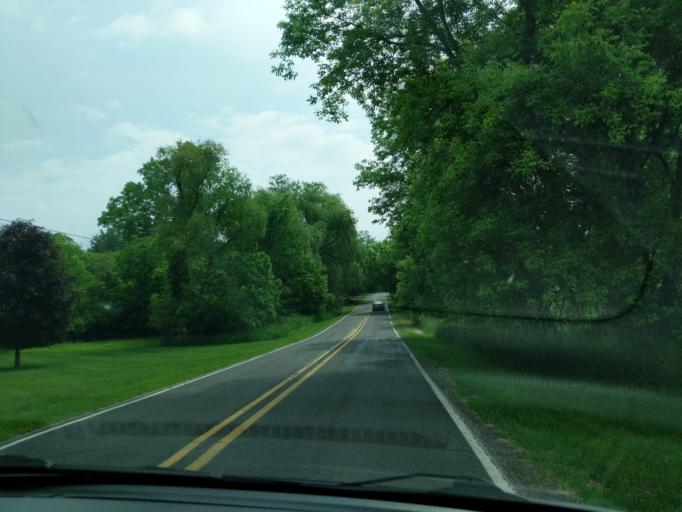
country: US
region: Michigan
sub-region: Ingham County
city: Williamston
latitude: 42.6938
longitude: -84.2674
